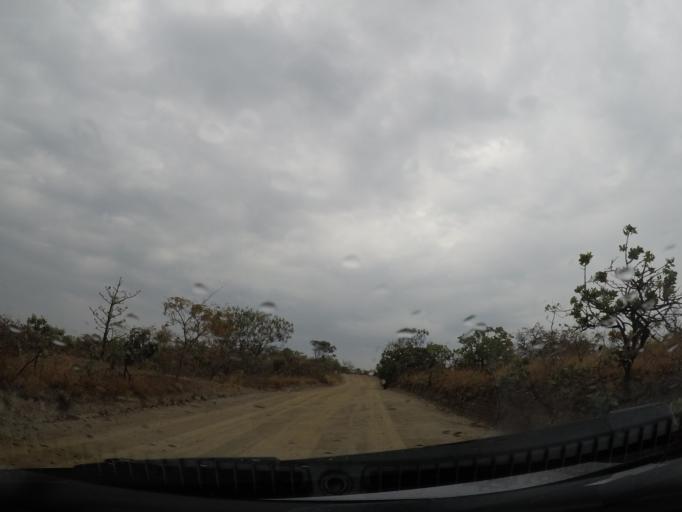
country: BR
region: Goias
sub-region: Pirenopolis
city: Pirenopolis
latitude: -15.8232
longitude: -48.9069
